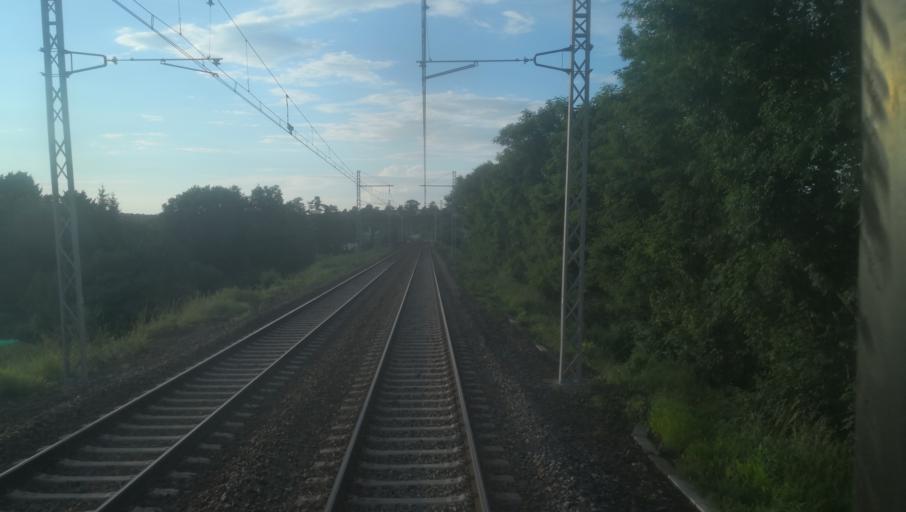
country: FR
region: Centre
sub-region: Departement de l'Indre
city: Argenton-sur-Creuse
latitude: 46.5826
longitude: 1.5252
